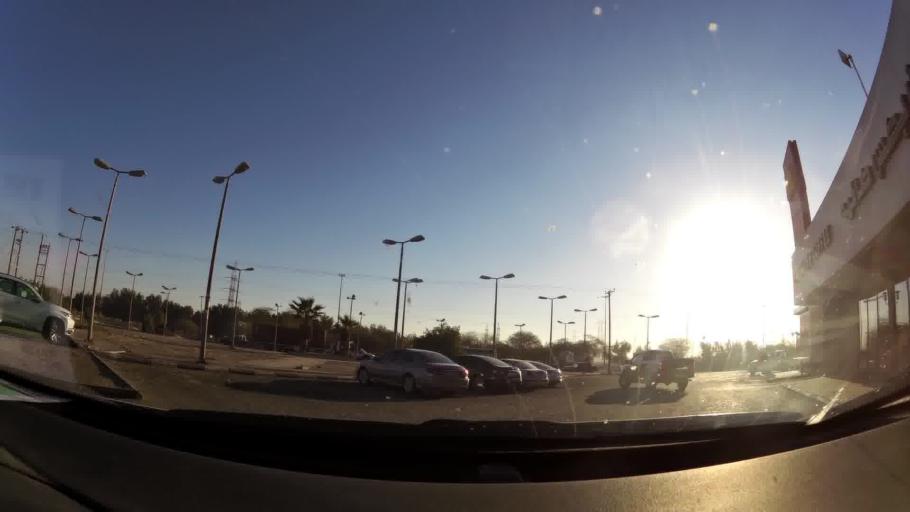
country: SA
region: Eastern Province
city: Al Khafji
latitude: 28.7316
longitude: 48.2847
